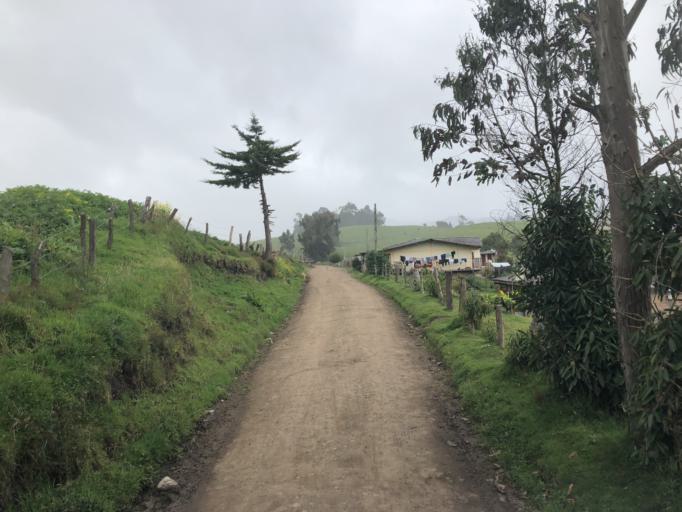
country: CO
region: Cauca
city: Totoro
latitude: 2.4664
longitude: -76.3327
